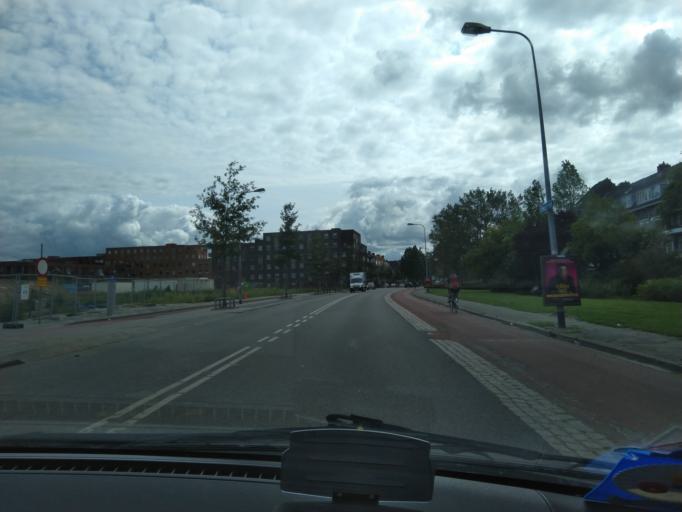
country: NL
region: Groningen
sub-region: Gemeente Groningen
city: Groningen
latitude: 53.2092
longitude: 6.5571
